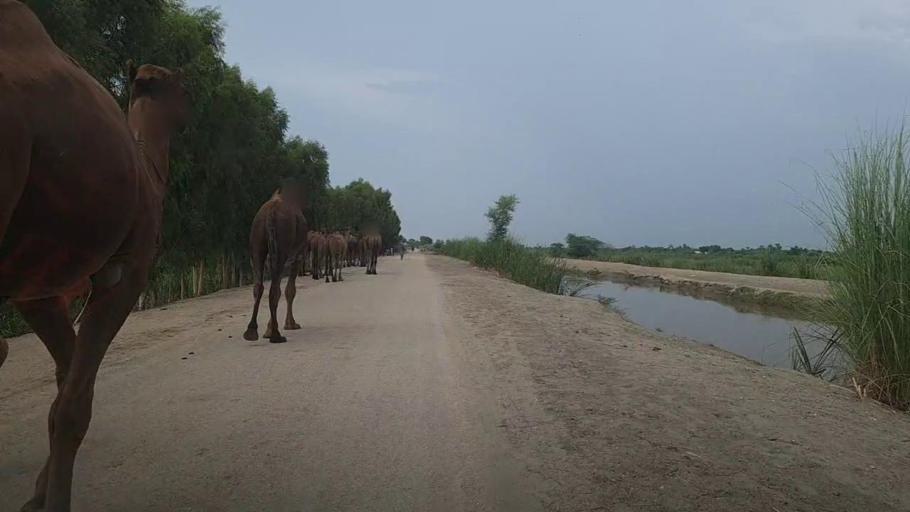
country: PK
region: Sindh
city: Karaundi
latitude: 26.9631
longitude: 68.4264
